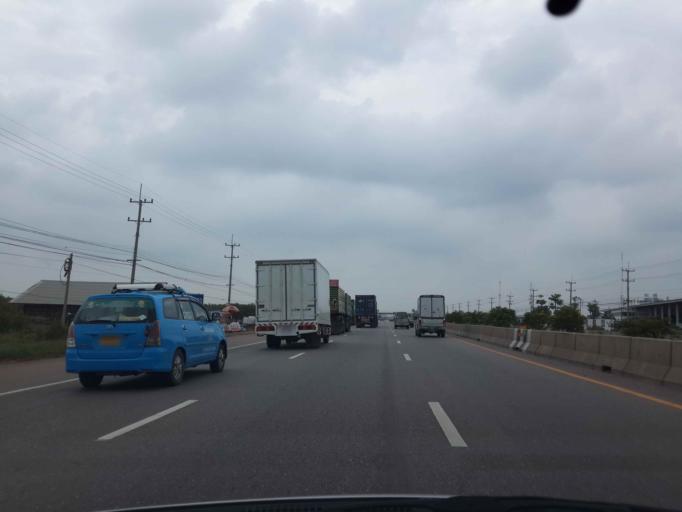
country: TH
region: Samut Sakhon
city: Ban Phaeo
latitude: 13.4715
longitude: 100.1126
